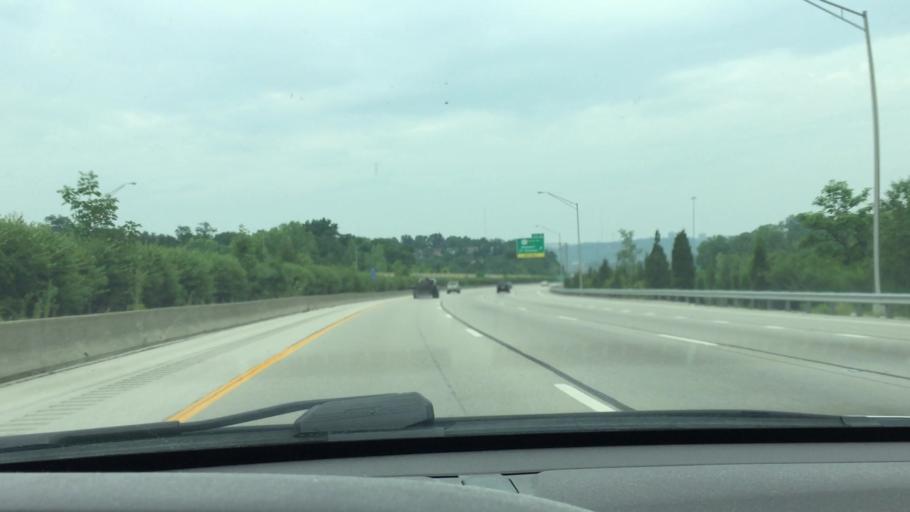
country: US
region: Kentucky
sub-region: Campbell County
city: Southgate
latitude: 39.0762
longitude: -84.4685
